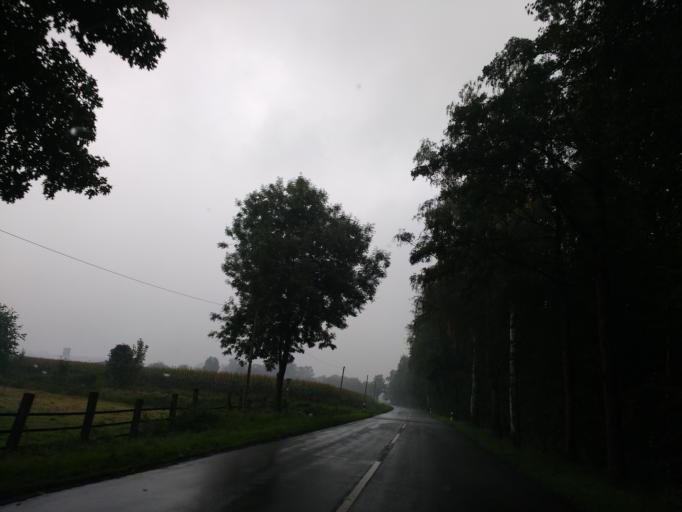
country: DE
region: North Rhine-Westphalia
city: Rietberg
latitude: 51.7619
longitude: 8.4865
